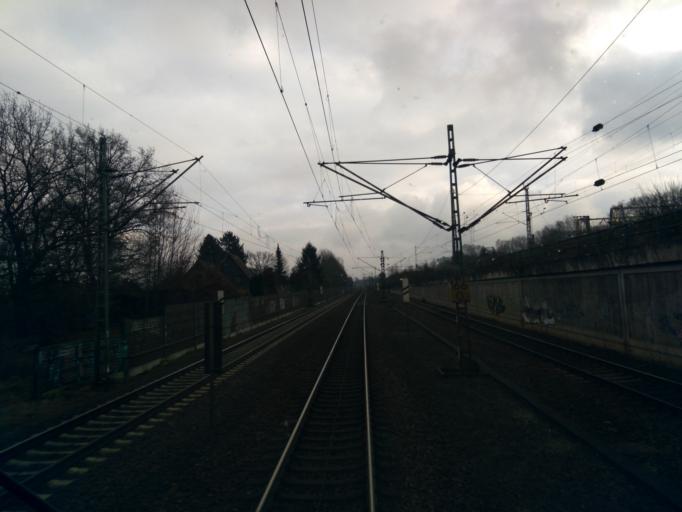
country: DE
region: Hamburg
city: Harburg
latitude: 53.4326
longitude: 10.0193
